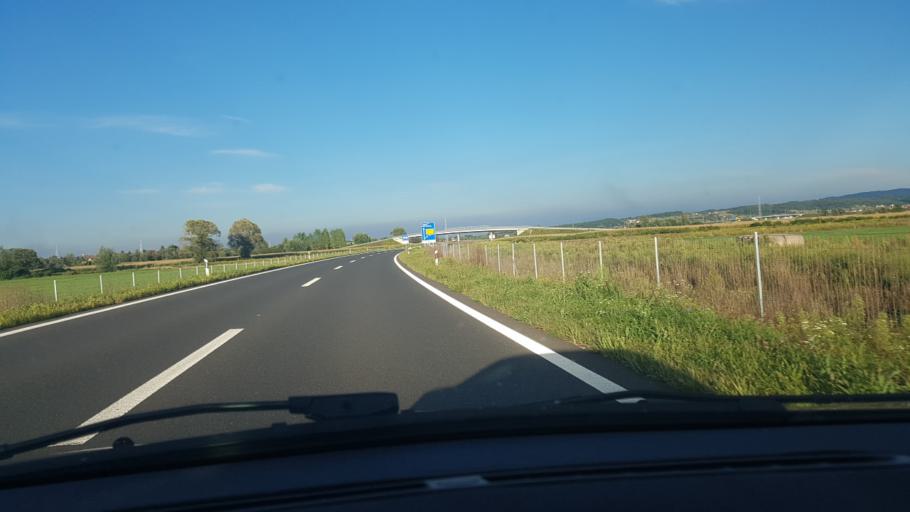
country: HR
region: Krapinsko-Zagorska
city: Selnica
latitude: 46.0405
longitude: 16.0590
